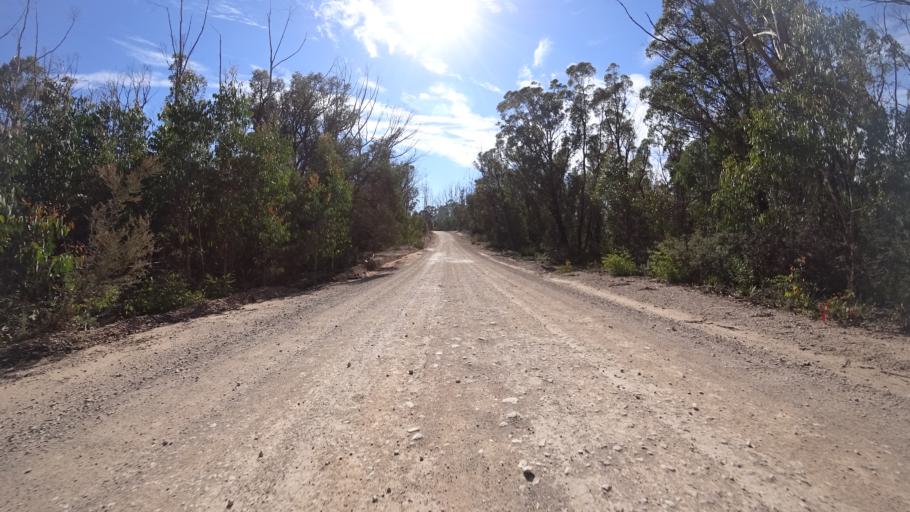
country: AU
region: New South Wales
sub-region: Lithgow
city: Lithgow
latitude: -33.4322
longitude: 150.1918
